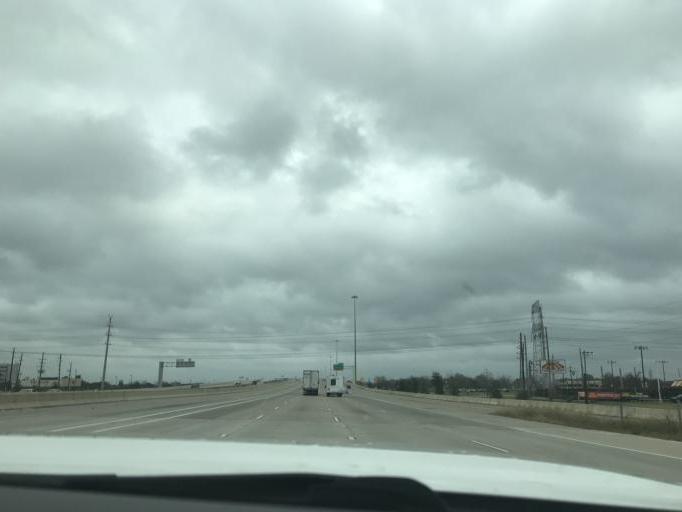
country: US
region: Texas
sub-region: Fort Bend County
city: Greatwood
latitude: 29.5603
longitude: -95.6964
